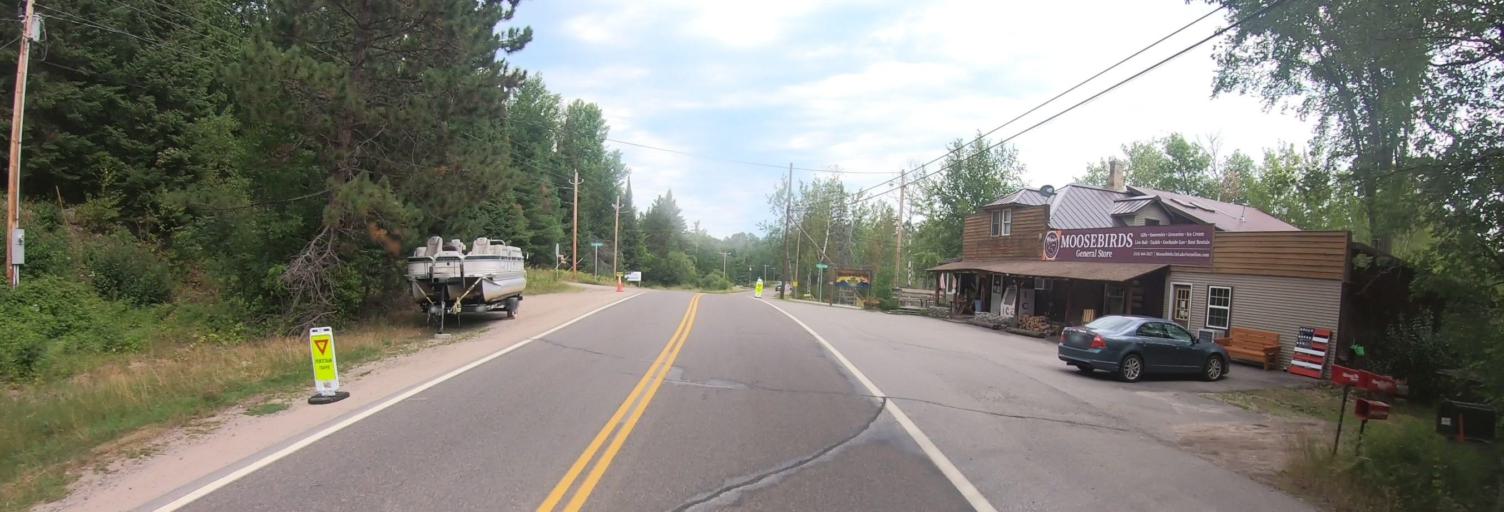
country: US
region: Minnesota
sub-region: Saint Louis County
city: Mountain Iron
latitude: 47.9461
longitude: -92.6640
